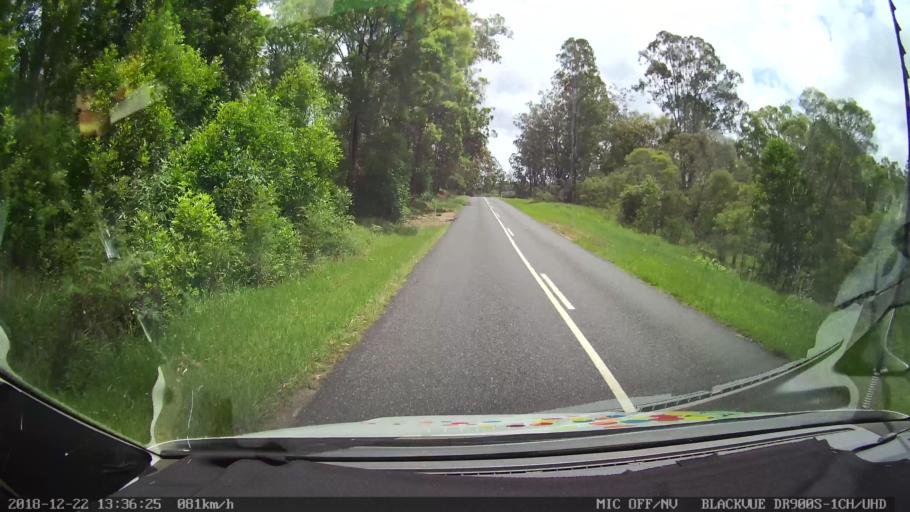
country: AU
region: New South Wales
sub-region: Clarence Valley
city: Coutts Crossing
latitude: -29.8798
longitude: 152.7951
